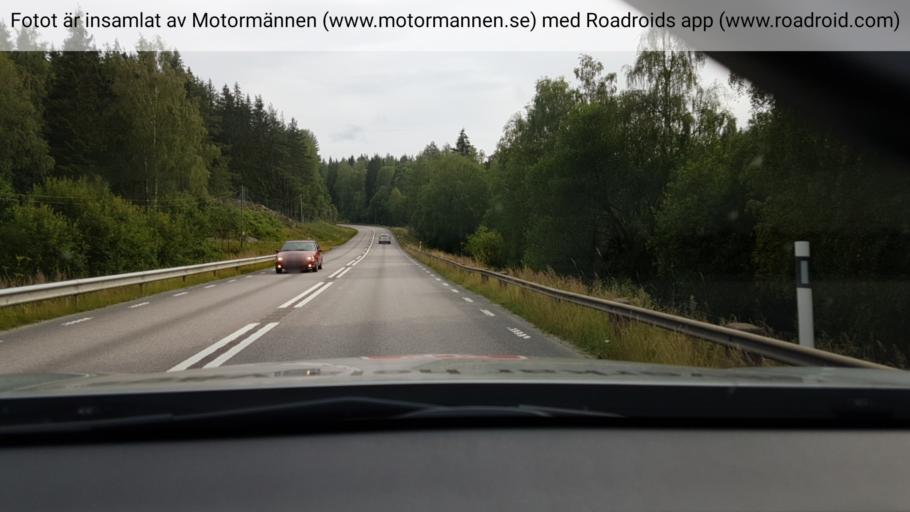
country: SE
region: Vaestra Goetaland
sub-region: Bengtsfors Kommun
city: Billingsfors
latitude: 59.0070
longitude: 12.2705
